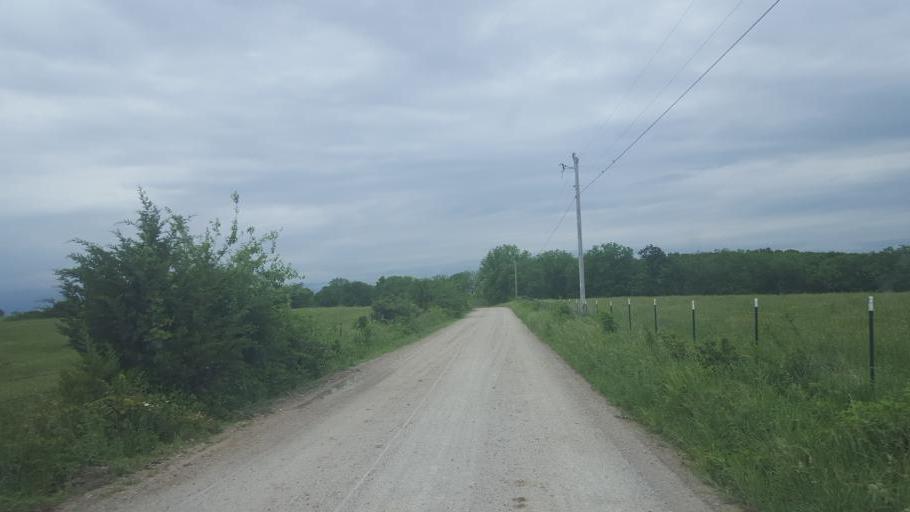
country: US
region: Missouri
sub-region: Moniteau County
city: California
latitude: 38.7551
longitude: -92.6056
